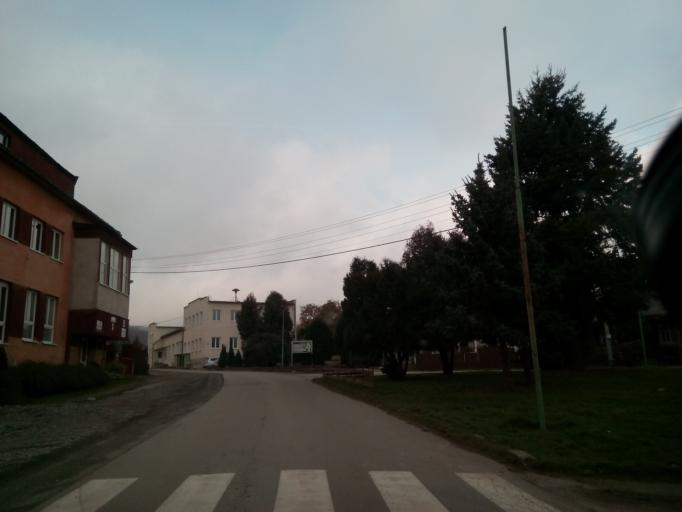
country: SK
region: Kosicky
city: Kosice
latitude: 48.7277
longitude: 21.1420
